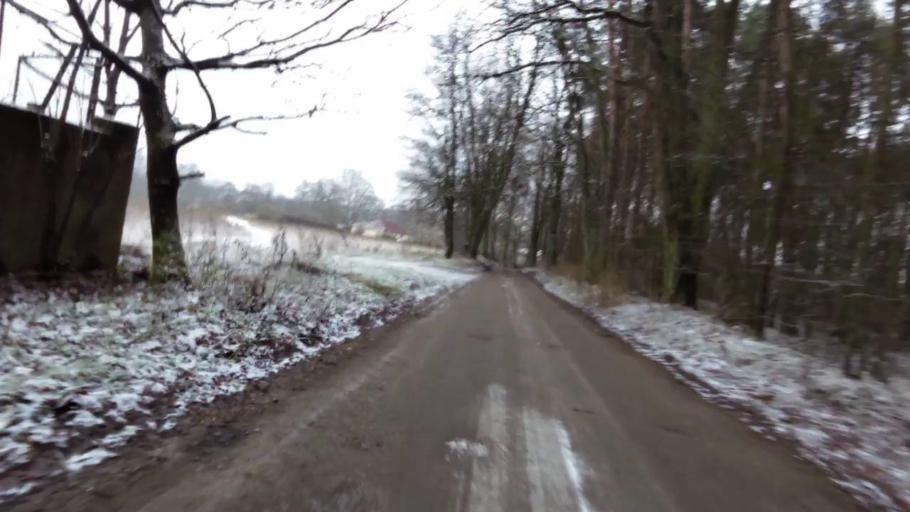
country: PL
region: West Pomeranian Voivodeship
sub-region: Powiat walecki
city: Walcz
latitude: 53.3033
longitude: 16.4736
